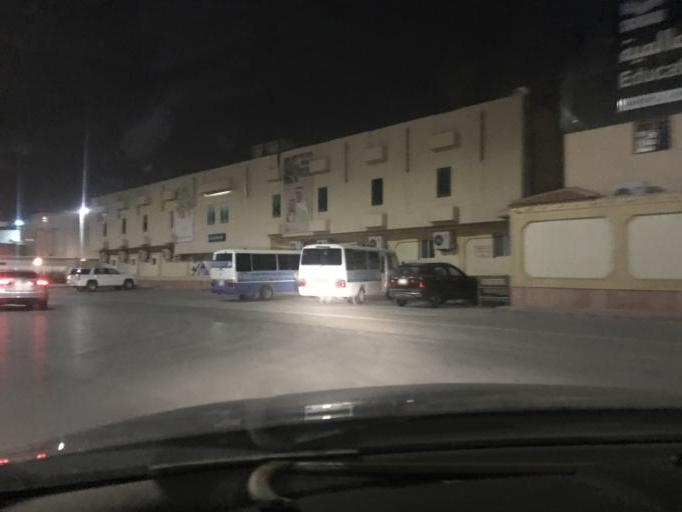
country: SA
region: Ar Riyad
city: Riyadh
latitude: 24.7311
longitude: 46.7776
